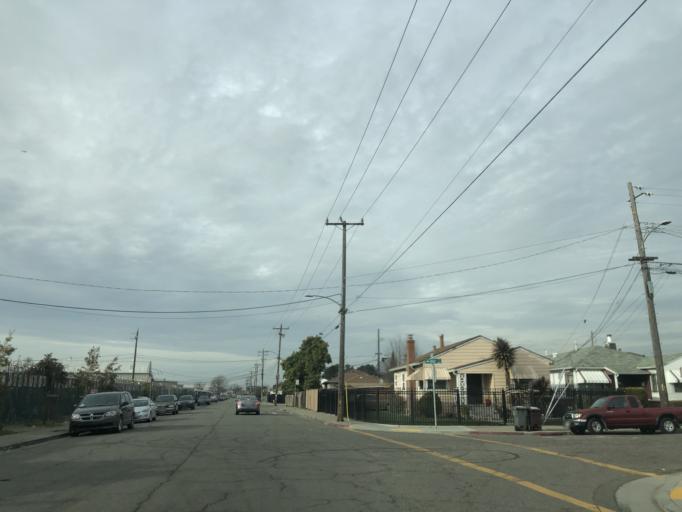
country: US
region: California
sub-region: Alameda County
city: San Leandro
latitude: 37.7382
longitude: -122.1740
